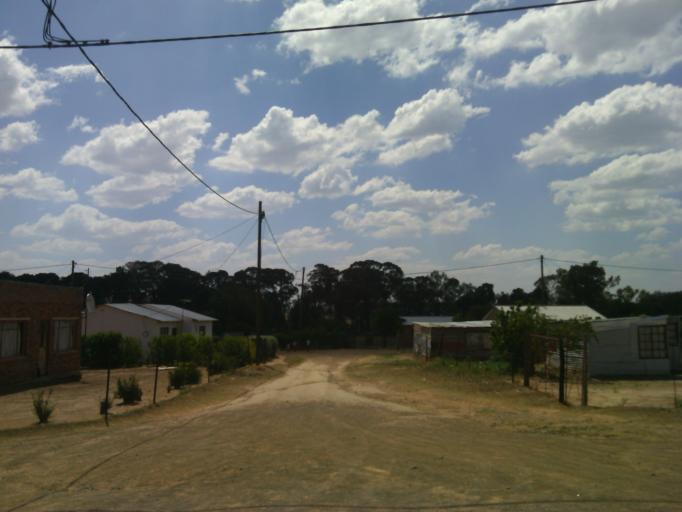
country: ZA
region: Orange Free State
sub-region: Xhariep District Municipality
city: Dewetsdorp
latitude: -29.5785
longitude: 26.6795
